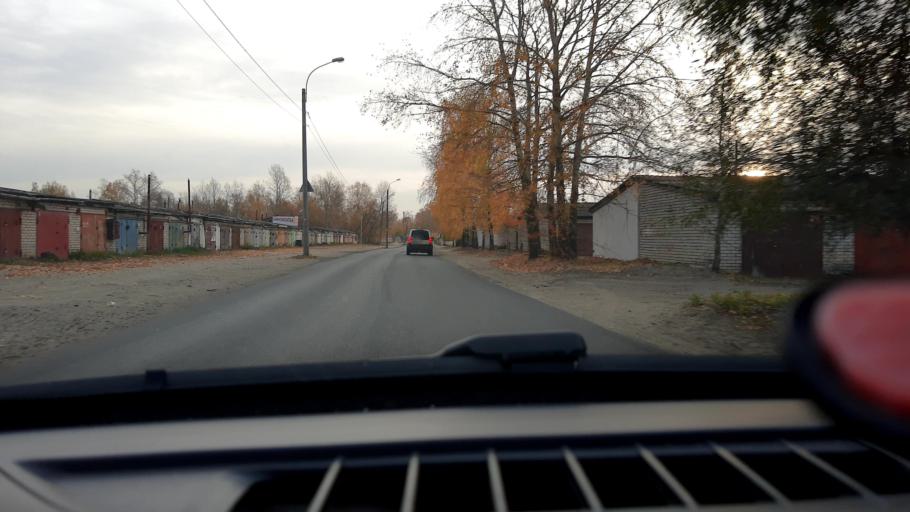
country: RU
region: Nizjnij Novgorod
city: Gorbatovka
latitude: 56.3308
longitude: 43.8154
